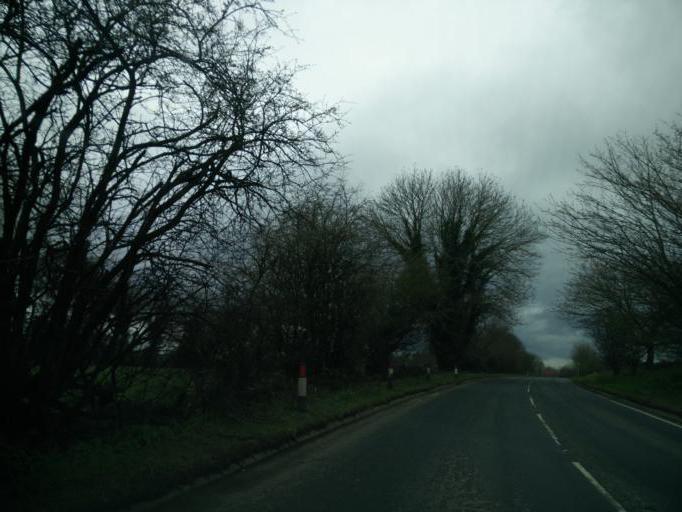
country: GB
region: England
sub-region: County Durham
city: Wolsingham
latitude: 54.7277
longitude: -1.9167
